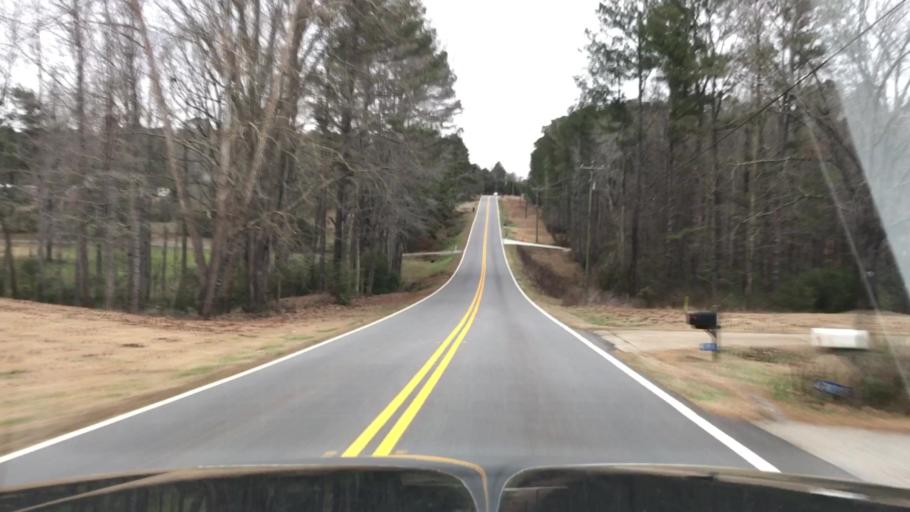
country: US
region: Georgia
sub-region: Barrow County
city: Auburn
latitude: 33.8994
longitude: -83.7948
